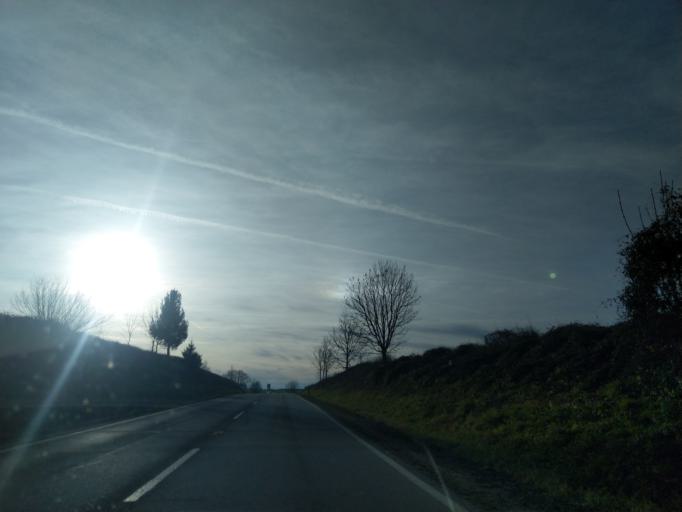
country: DE
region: Bavaria
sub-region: Lower Bavaria
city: Wallerfing
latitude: 48.6749
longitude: 12.8776
